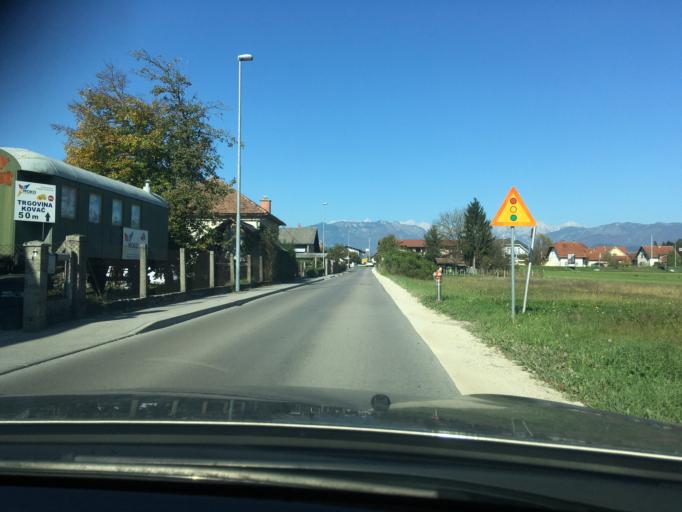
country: SI
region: Domzale
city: Vir
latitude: 46.1461
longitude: 14.6080
